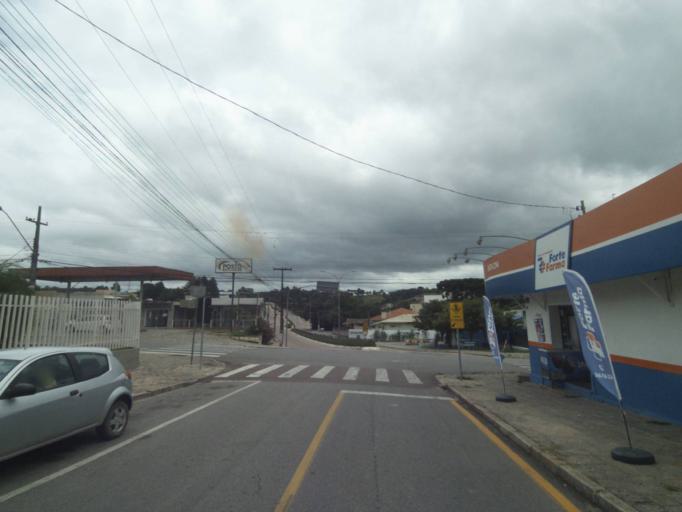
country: BR
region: Parana
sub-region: Campina Grande Do Sul
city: Campina Grande do Sul
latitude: -25.3049
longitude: -49.0539
